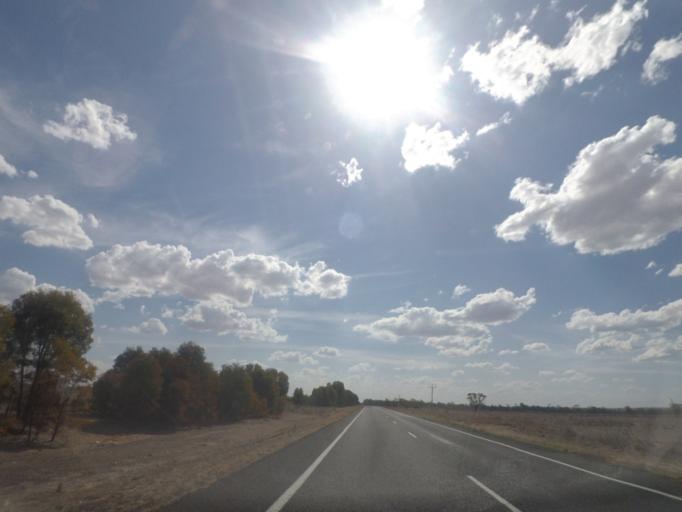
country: AU
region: New South Wales
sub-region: Moree Plains
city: Boggabilla
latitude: -28.4149
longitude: 151.1292
